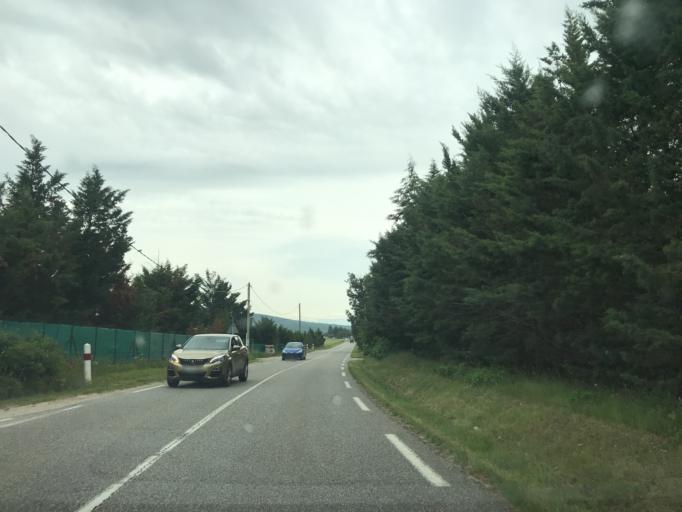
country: FR
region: Provence-Alpes-Cote d'Azur
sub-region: Departement du Var
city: Rians
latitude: 43.6301
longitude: 5.7729
